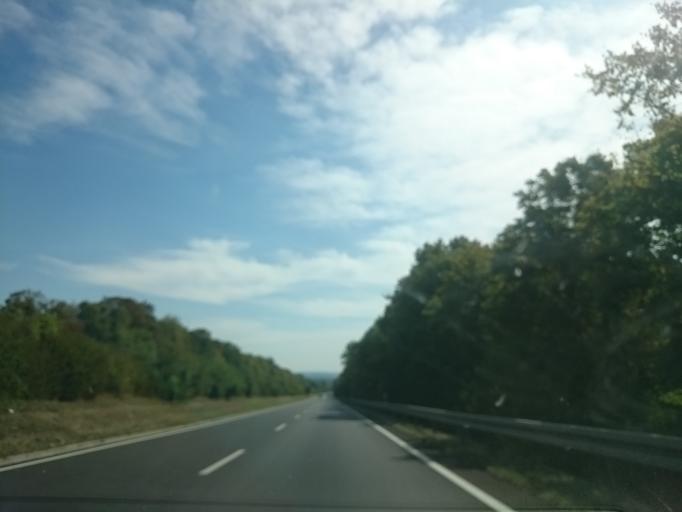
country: DE
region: Bavaria
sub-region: Swabia
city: Donauwoerth
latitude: 48.7185
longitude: 10.7887
